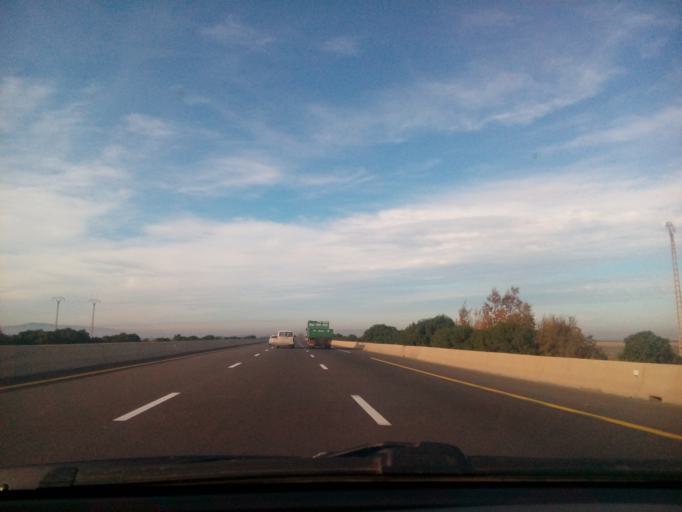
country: DZ
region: Mascara
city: Sig
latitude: 35.5911
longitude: -0.0587
